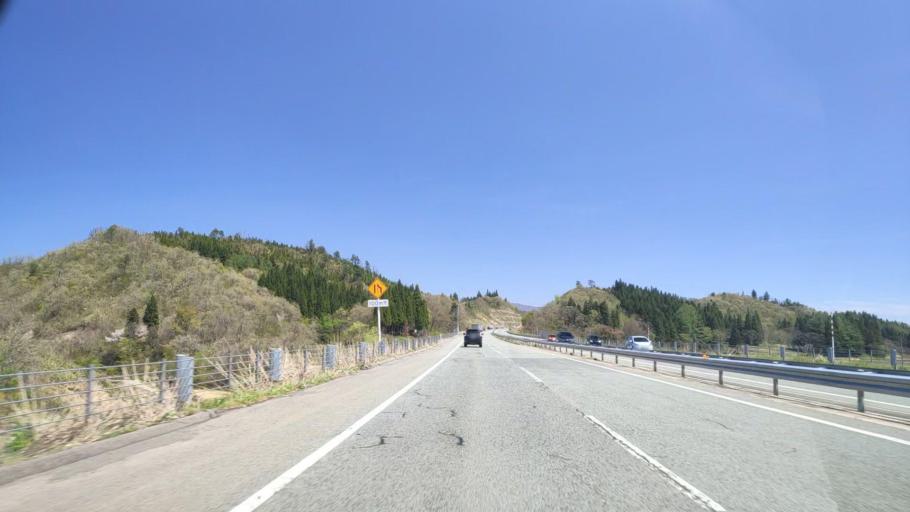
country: JP
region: Yamagata
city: Obanazawa
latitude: 38.6668
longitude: 140.3416
